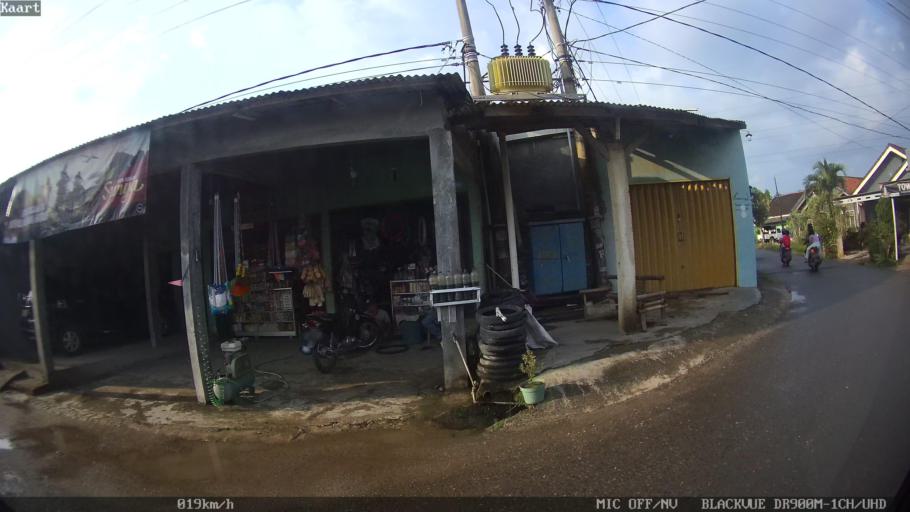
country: ID
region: Lampung
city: Kedaton
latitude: -5.3883
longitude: 105.3189
